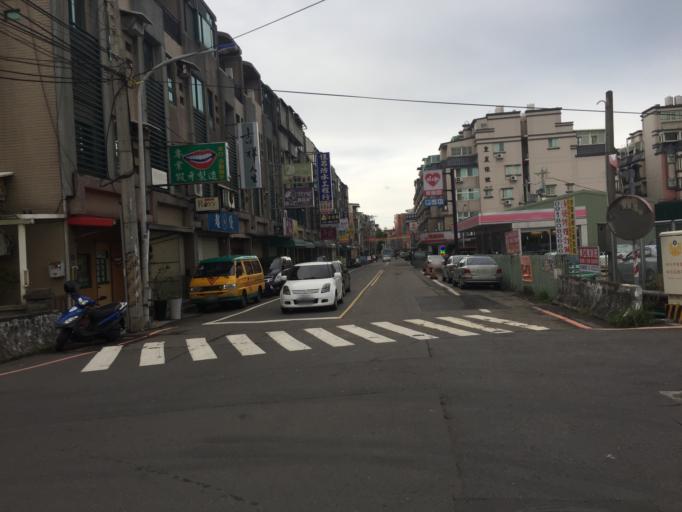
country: TW
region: Taiwan
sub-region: Hsinchu
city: Hsinchu
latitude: 24.7905
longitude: 120.9239
